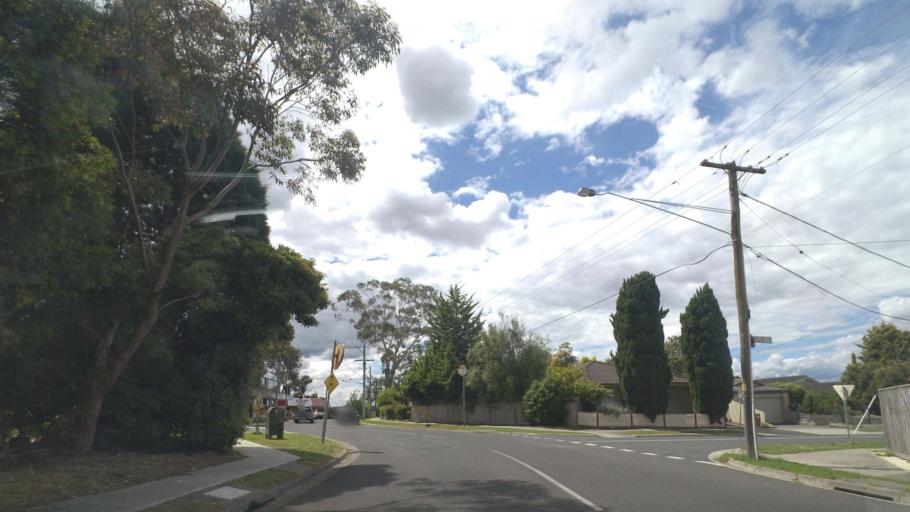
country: AU
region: Victoria
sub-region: Knox
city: Wantirna
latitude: -37.8482
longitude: 145.2338
